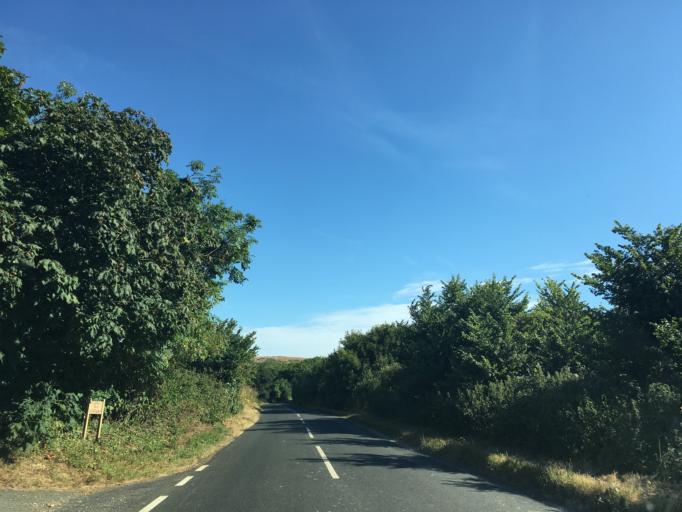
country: GB
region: England
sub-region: Isle of Wight
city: Chale
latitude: 50.6315
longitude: -1.3167
